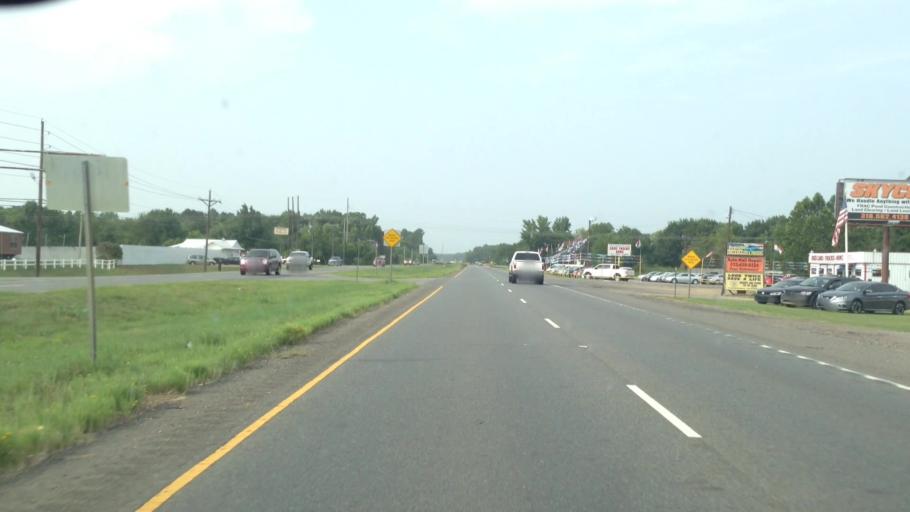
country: US
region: Louisiana
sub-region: De Soto Parish
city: Stonewall
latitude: 32.3796
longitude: -93.8203
